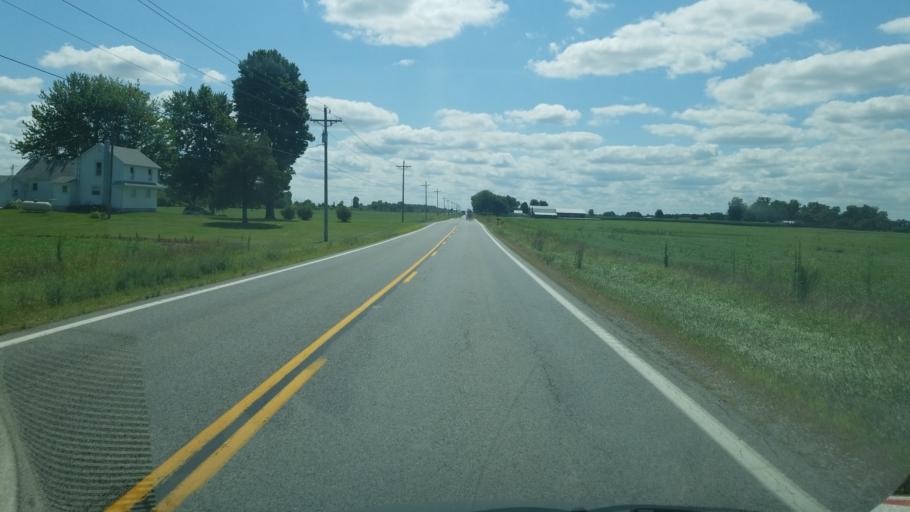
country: US
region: Ohio
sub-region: Fulton County
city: Delta
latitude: 41.6343
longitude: -84.0347
